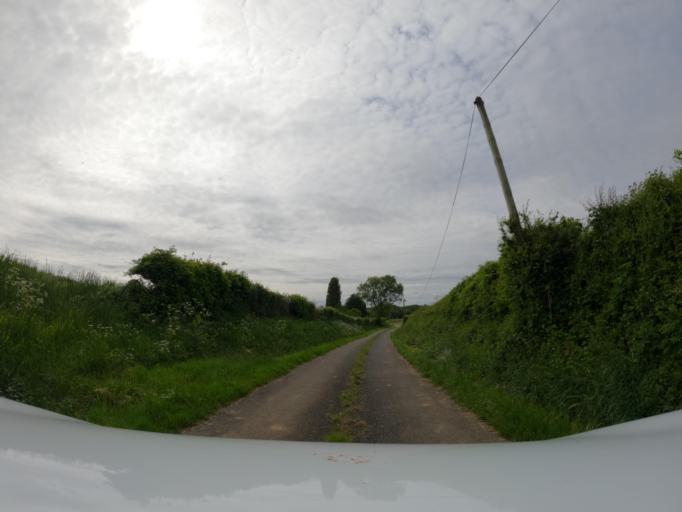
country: FR
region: Pays de la Loire
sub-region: Departement de la Vendee
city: Saint-Hilaire-des-Loges
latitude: 46.4965
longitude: -0.6696
